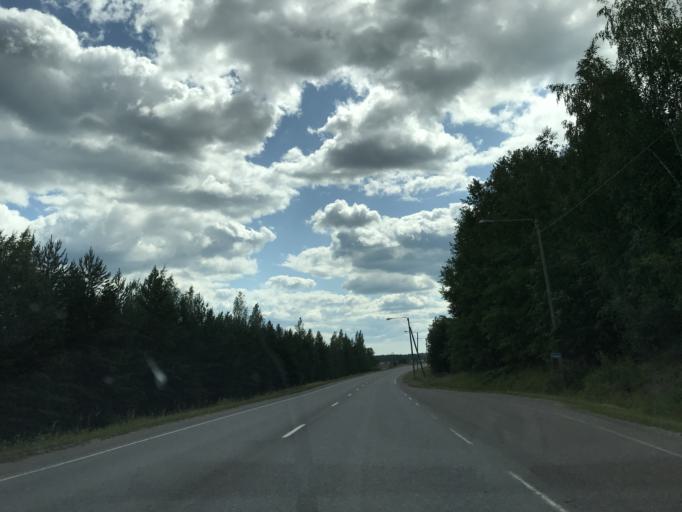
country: FI
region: Uusimaa
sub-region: Helsinki
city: Maentsaelae
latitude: 60.6657
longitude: 25.3502
